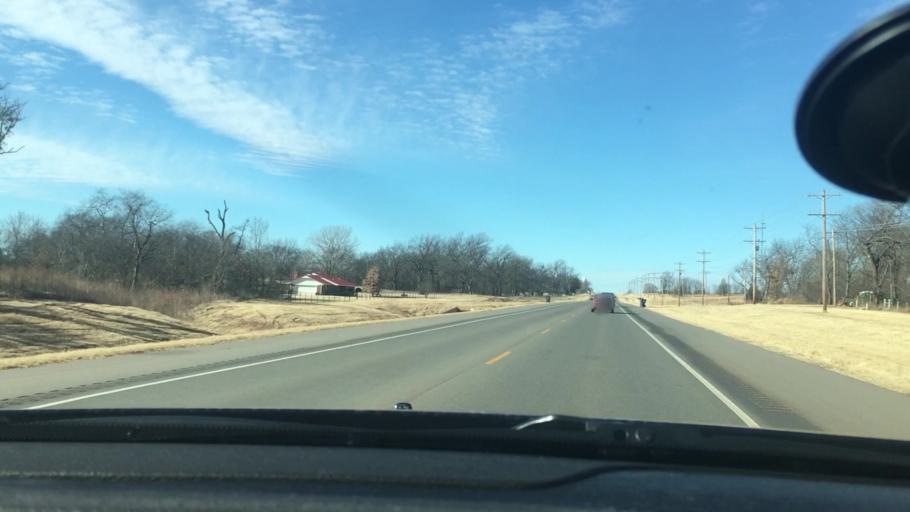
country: US
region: Oklahoma
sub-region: Cleveland County
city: Lexington
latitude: 35.0149
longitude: -97.2551
